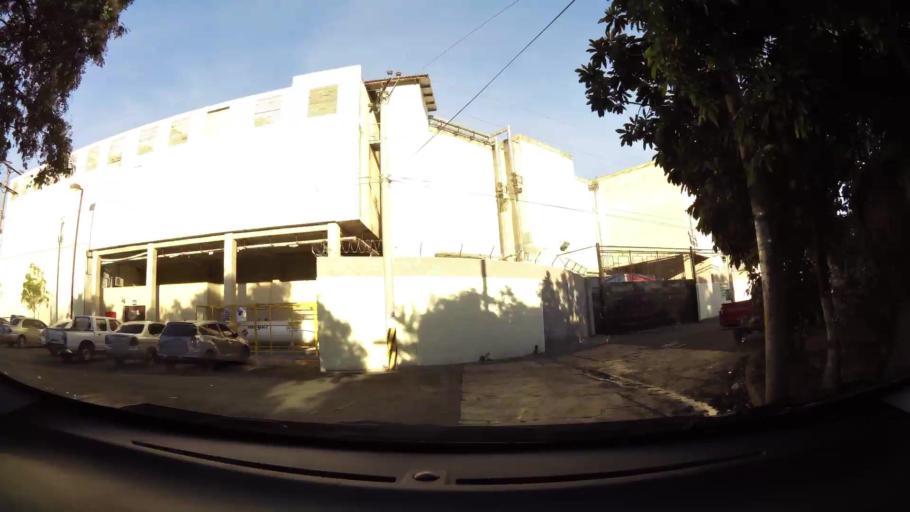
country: SV
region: San Miguel
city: San Miguel
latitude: 13.4610
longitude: -88.1663
